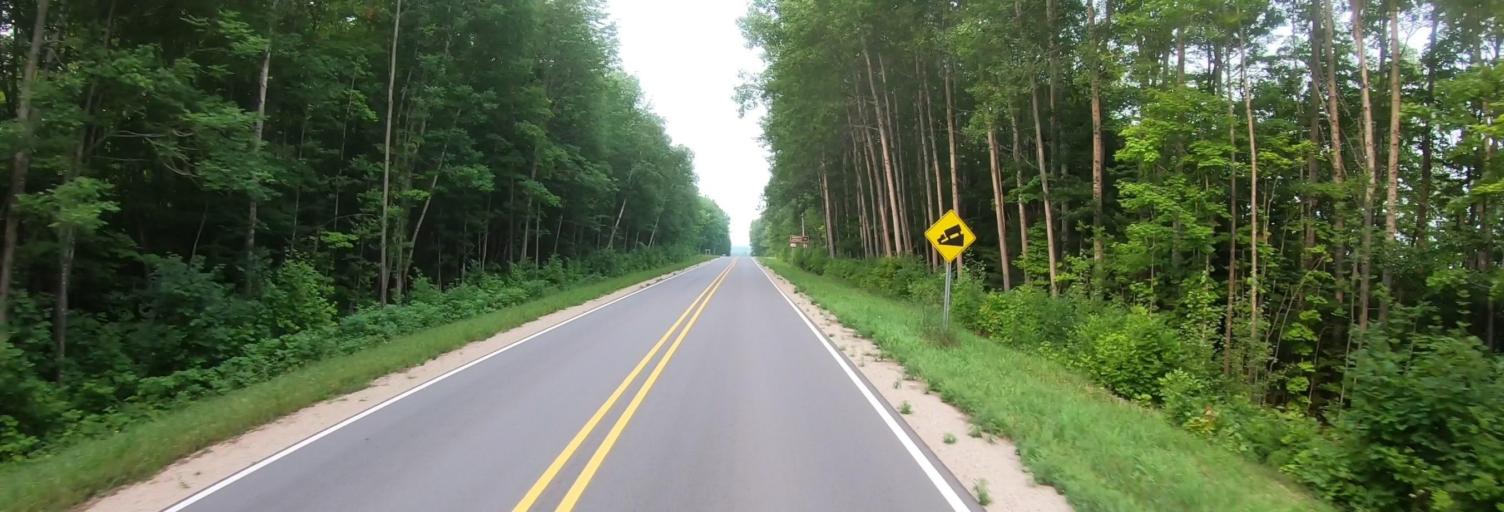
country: US
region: Michigan
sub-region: Luce County
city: Newberry
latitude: 46.4741
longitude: -84.9546
